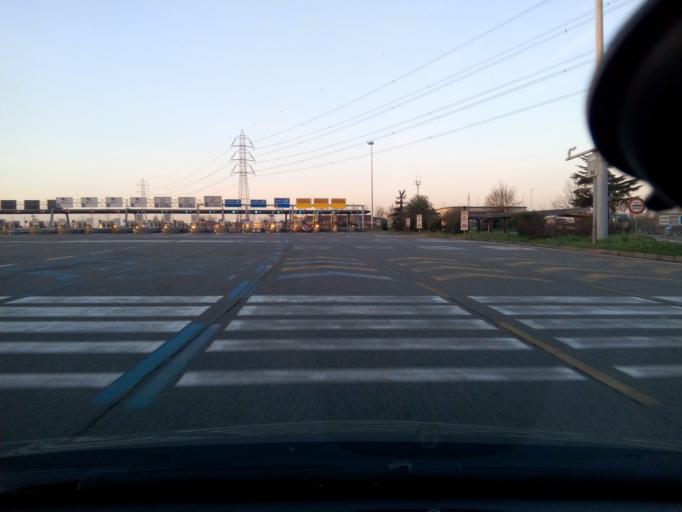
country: IT
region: Lombardy
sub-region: Citta metropolitana di Milano
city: Passirana
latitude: 45.5425
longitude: 9.0585
